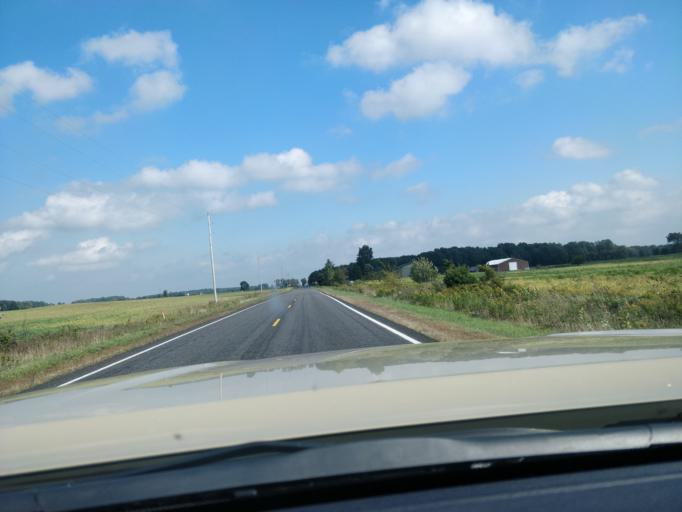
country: US
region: Michigan
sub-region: Ionia County
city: Saranac
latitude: 42.8862
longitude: -85.1396
